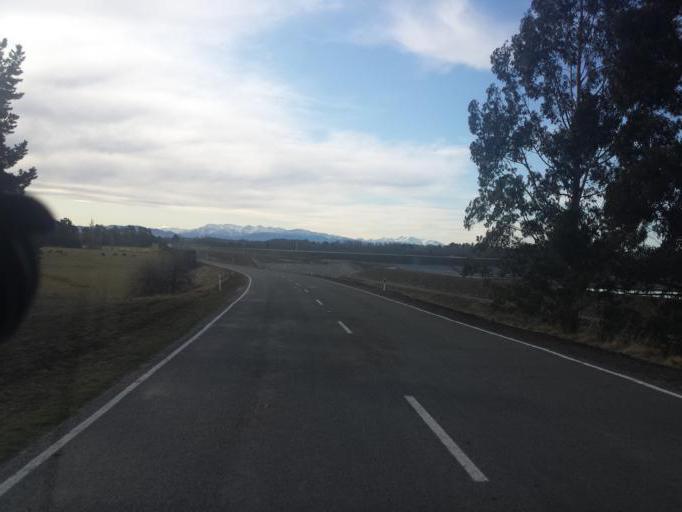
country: NZ
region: Canterbury
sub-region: Timaru District
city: Pleasant Point
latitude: -43.9944
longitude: 171.2957
